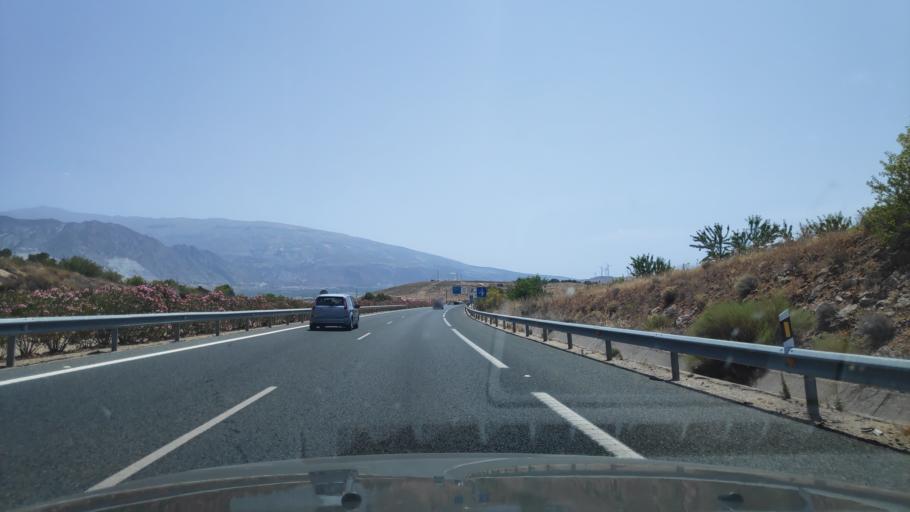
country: ES
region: Andalusia
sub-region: Provincia de Granada
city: Padul
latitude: 36.9905
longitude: -3.6146
